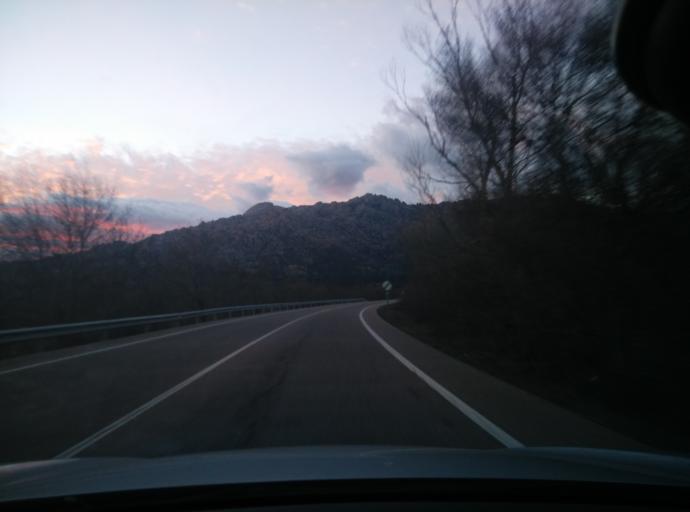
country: ES
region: Madrid
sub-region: Provincia de Madrid
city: Manzanares el Real
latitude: 40.7384
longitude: -3.8229
